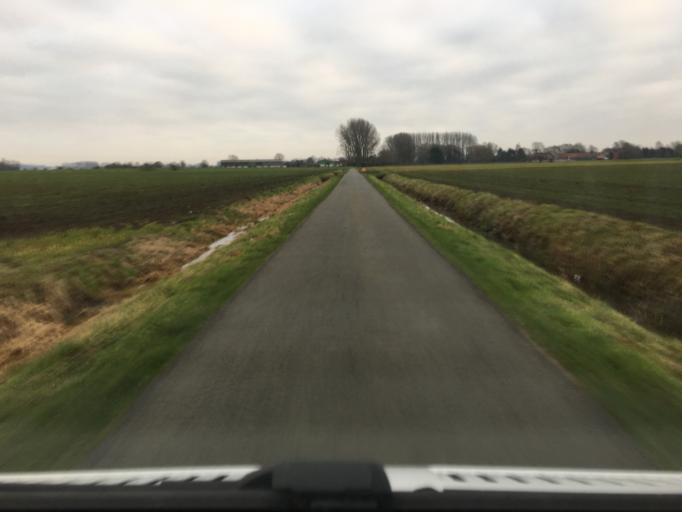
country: FR
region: Nord-Pas-de-Calais
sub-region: Departement du Nord
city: Comines
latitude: 50.7486
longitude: 3.0168
